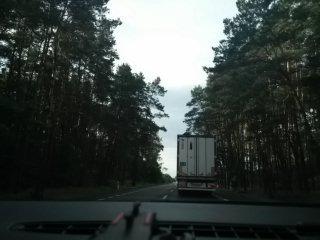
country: PL
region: Subcarpathian Voivodeship
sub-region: Powiat nizanski
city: Jarocin
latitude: 50.6326
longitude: 22.2865
